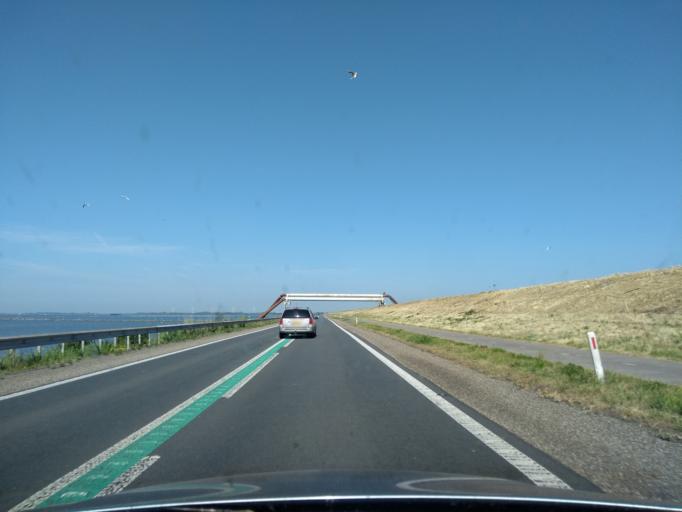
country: NL
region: North Holland
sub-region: Gemeente Enkhuizen
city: Enkhuizen
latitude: 52.6778
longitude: 5.3522
